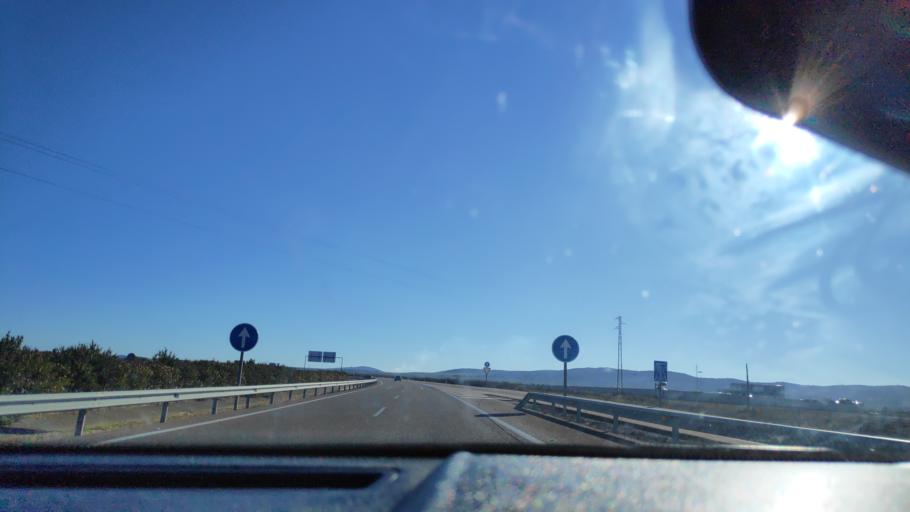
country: ES
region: Extremadura
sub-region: Provincia de Badajoz
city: Villafranca de los Barros
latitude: 38.5487
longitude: -6.3642
